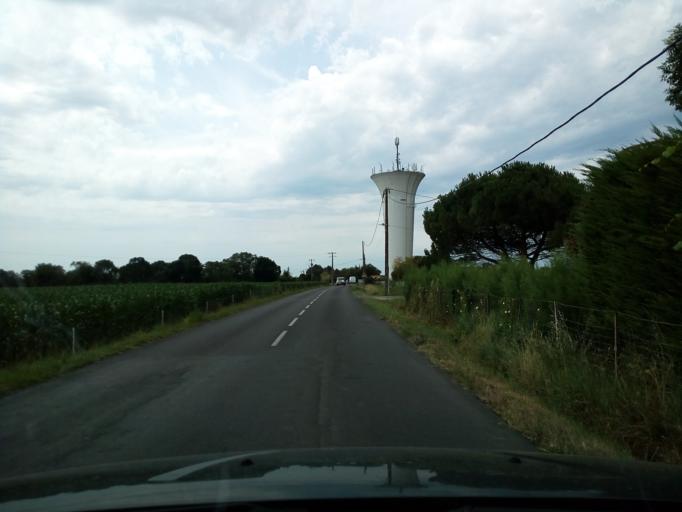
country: FR
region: Poitou-Charentes
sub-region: Departement de la Charente-Maritime
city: Dolus-d'Oleron
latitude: 45.9333
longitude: -1.3141
